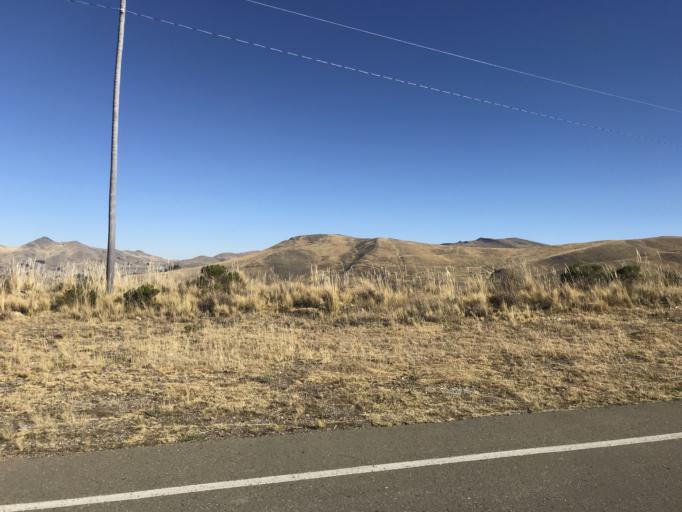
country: PE
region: Puno
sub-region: Yunguyo
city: Yunguyo
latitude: -16.1795
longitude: -68.9826
